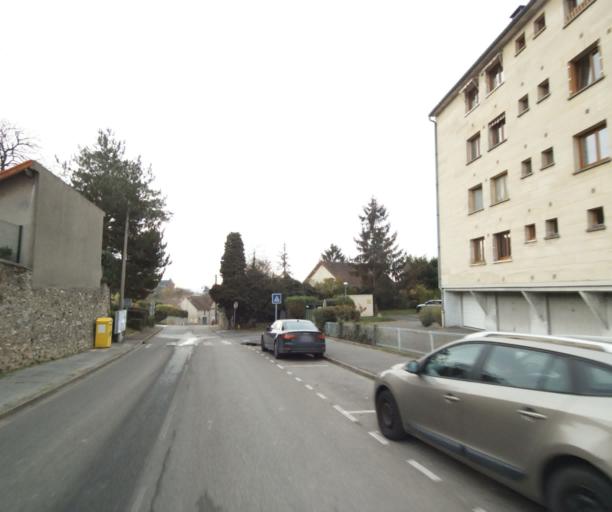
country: FR
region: Ile-de-France
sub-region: Departement des Yvelines
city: Triel-sur-Seine
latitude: 48.9851
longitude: 2.0034
